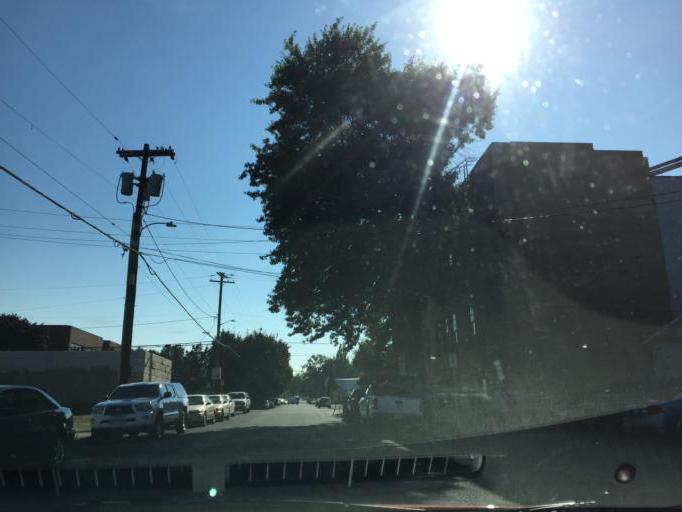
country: US
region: Oregon
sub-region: Multnomah County
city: Portland
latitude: 45.5215
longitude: -122.6575
